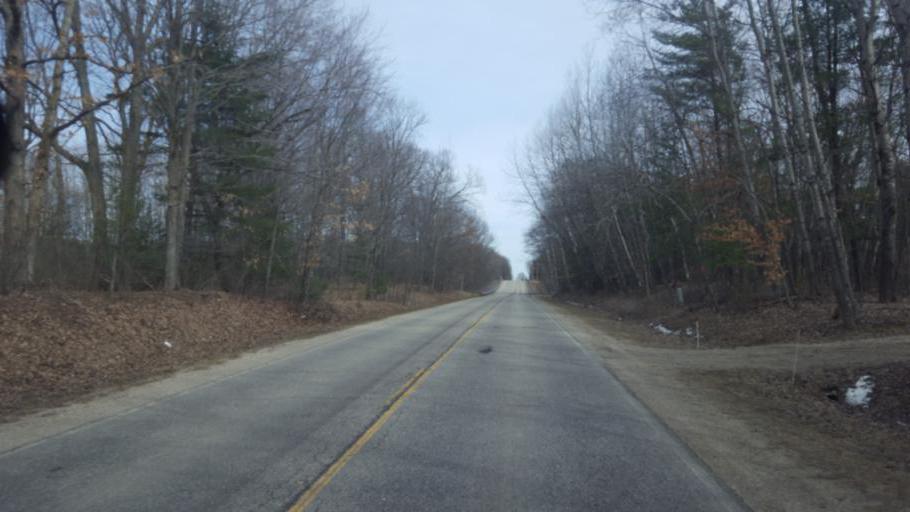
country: US
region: Michigan
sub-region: Isabella County
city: Lake Isabella
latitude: 43.6611
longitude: -85.0910
